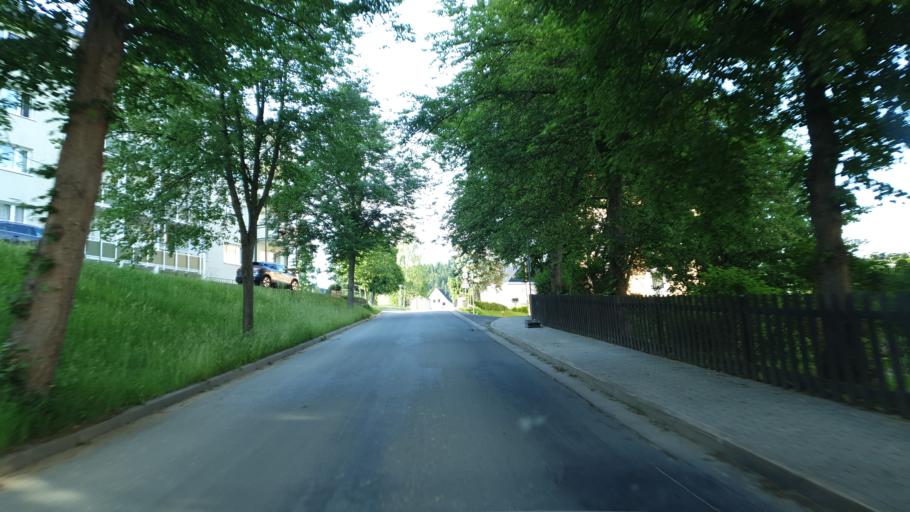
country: DE
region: Saxony
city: Klingenthal
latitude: 50.3608
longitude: 12.4597
